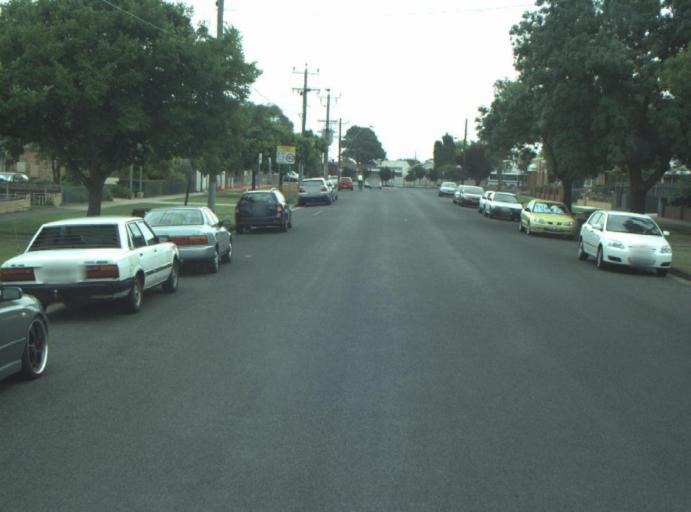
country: AU
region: Victoria
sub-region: Greater Geelong
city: East Geelong
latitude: -38.1634
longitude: 144.3750
